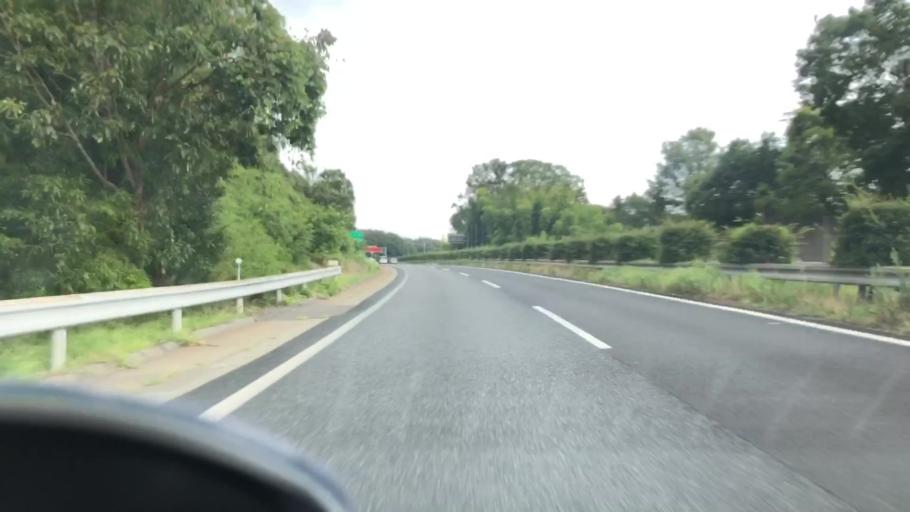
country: JP
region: Hyogo
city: Yashiro
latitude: 34.8930
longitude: 135.0850
